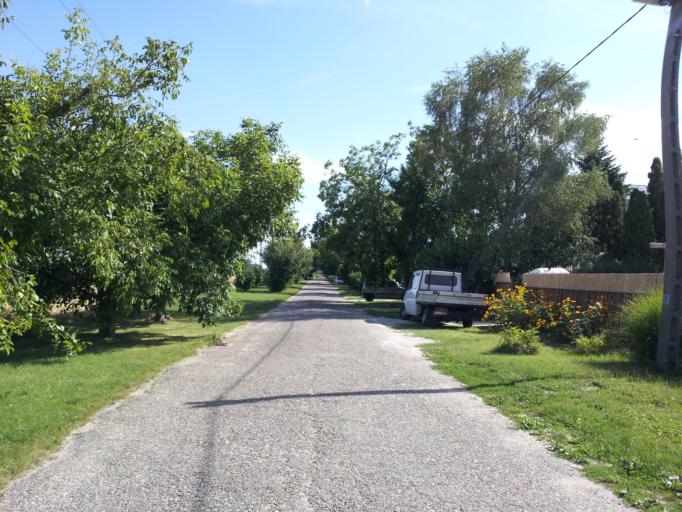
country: HU
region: Pest
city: Szigetcsep
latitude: 47.2409
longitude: 18.9784
